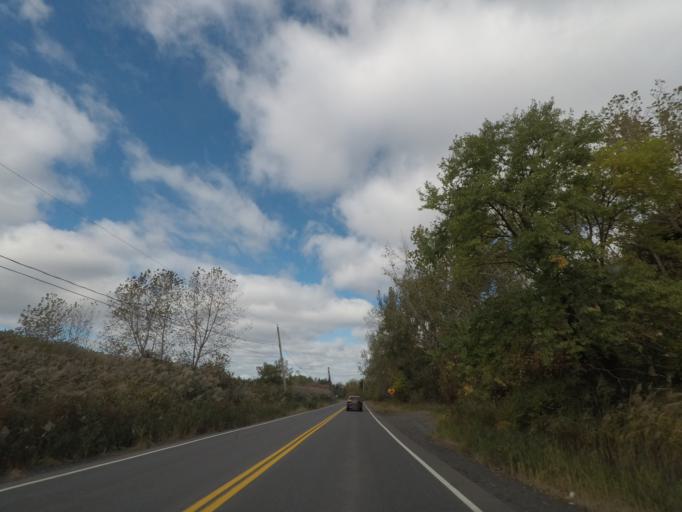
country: US
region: New York
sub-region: Albany County
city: Cohoes
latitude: 42.8152
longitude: -73.7289
